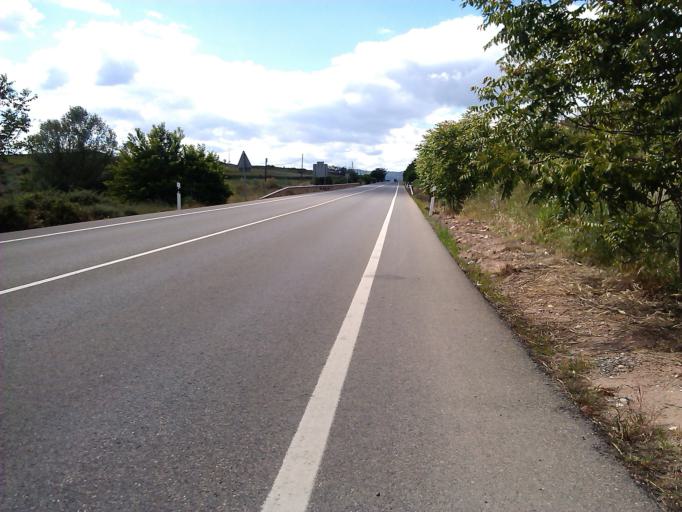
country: ES
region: La Rioja
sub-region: Provincia de La Rioja
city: Najera
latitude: 42.4276
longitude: -2.7475
